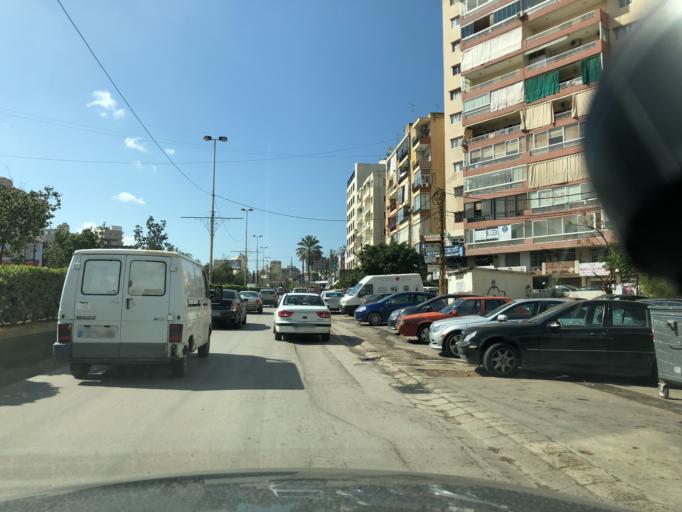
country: LB
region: Mont-Liban
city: Jdaidet el Matn
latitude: 33.8801
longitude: 35.5522
